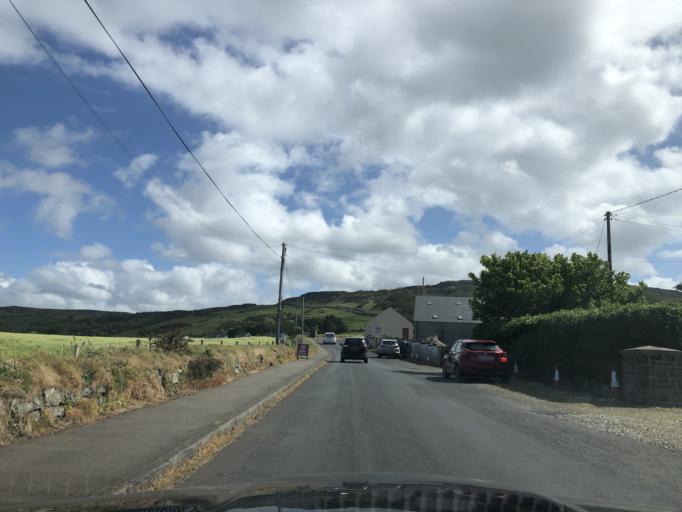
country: GB
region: Northern Ireland
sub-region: Moyle District
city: Ballycastle
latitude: 55.2393
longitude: -6.3662
